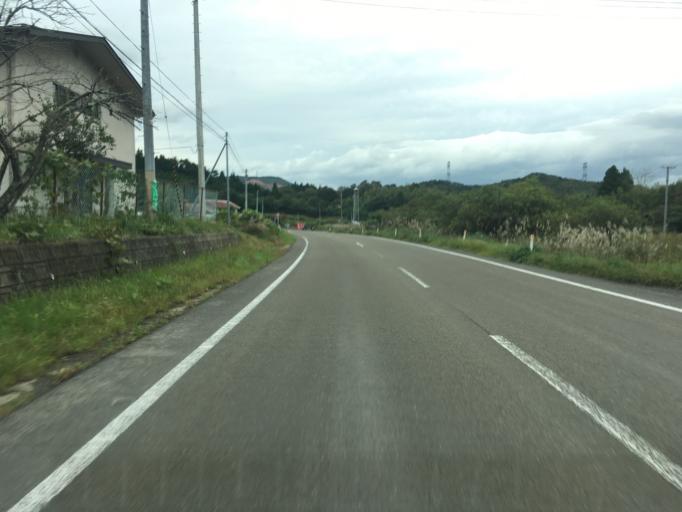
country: JP
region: Miyagi
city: Marumori
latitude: 37.8845
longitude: 140.7120
